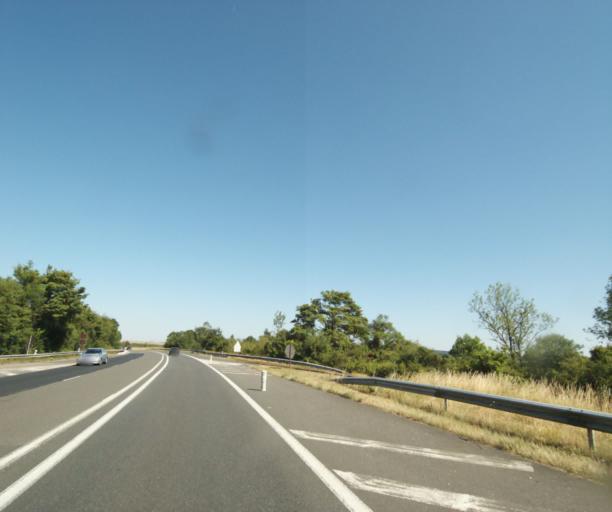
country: FR
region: Ile-de-France
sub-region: Departement de Seine-et-Marne
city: Moret-sur-Loing
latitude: 48.3651
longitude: 2.8076
